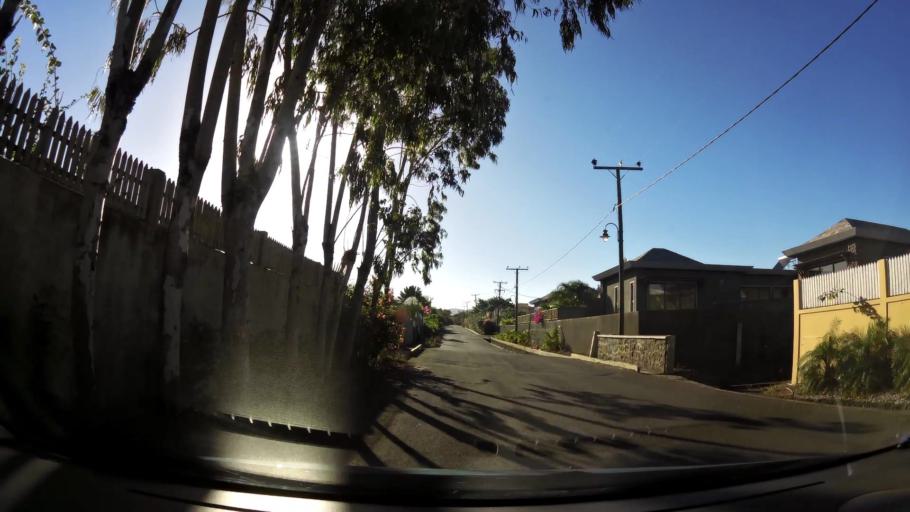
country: MU
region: Black River
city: Tamarin
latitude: -20.3357
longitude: 57.3770
